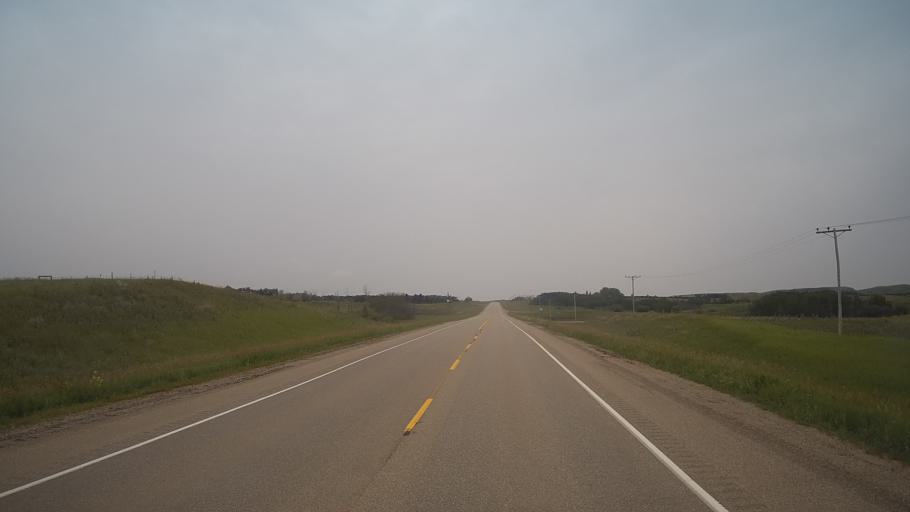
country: CA
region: Saskatchewan
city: Biggar
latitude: 52.0564
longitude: -107.8417
